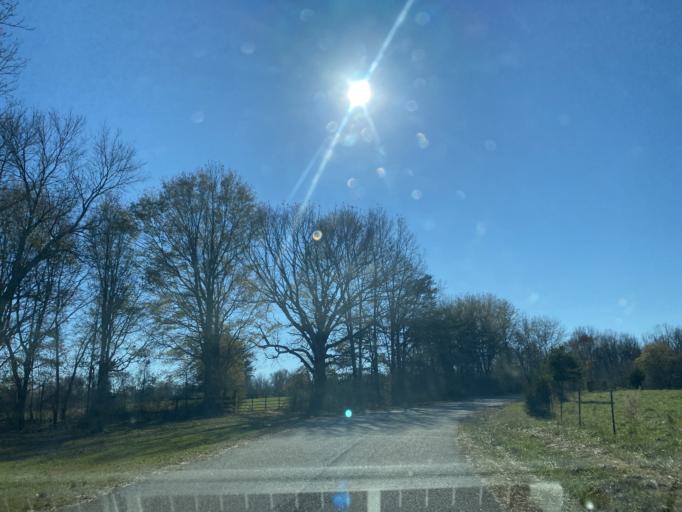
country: US
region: South Carolina
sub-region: Spartanburg County
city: Mayo
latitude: 35.1450
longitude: -81.7716
